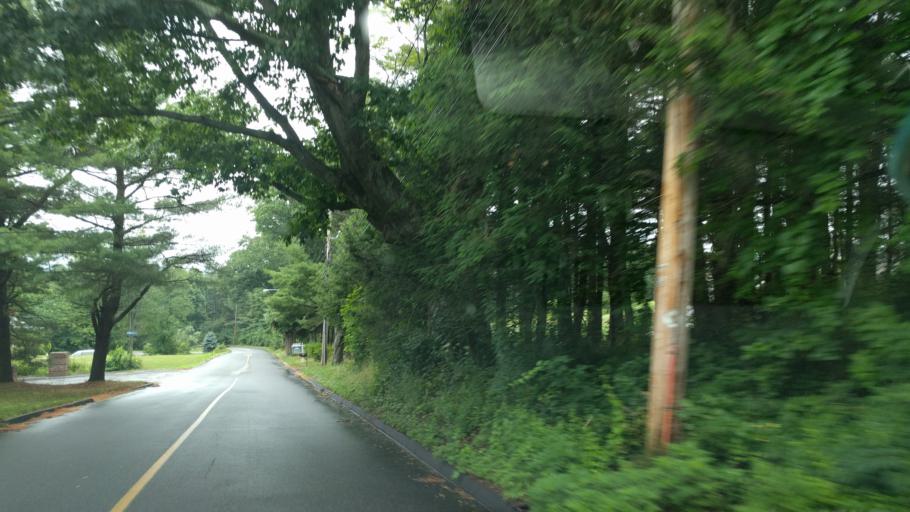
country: US
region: Massachusetts
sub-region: Worcester County
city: Auburn
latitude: 42.1938
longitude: -71.8189
